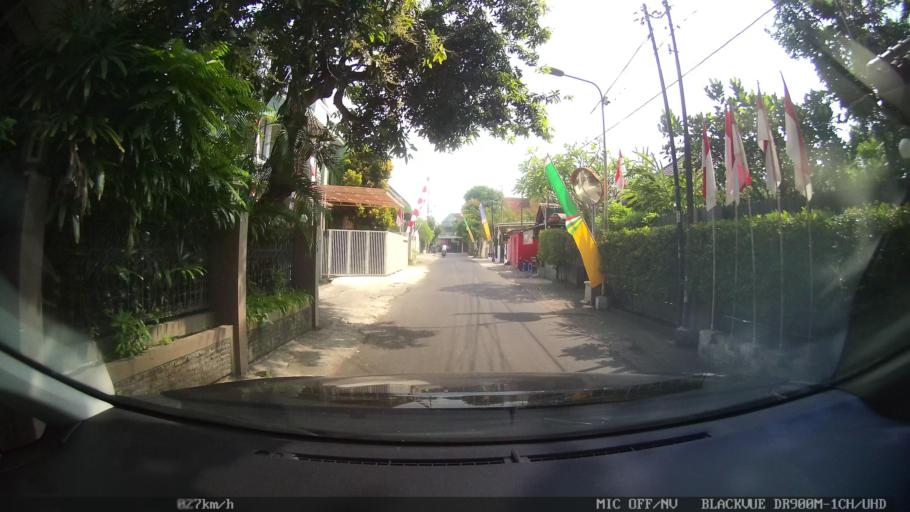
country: ID
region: Daerah Istimewa Yogyakarta
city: Yogyakarta
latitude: -7.8140
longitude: 110.3815
